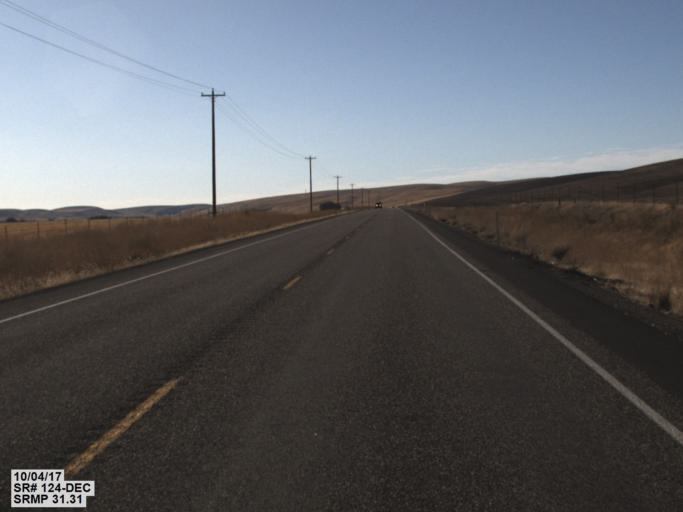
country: US
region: Washington
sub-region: Walla Walla County
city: Walla Walla
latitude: 46.2993
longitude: -118.4149
